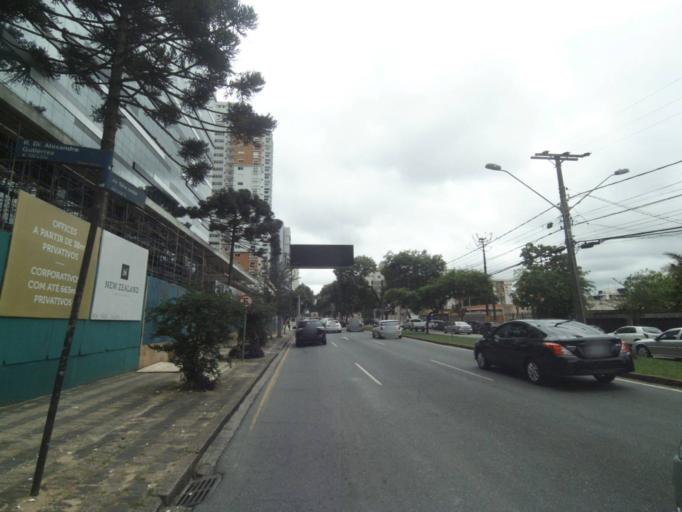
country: BR
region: Parana
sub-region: Curitiba
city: Curitiba
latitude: -25.4465
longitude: -49.2858
